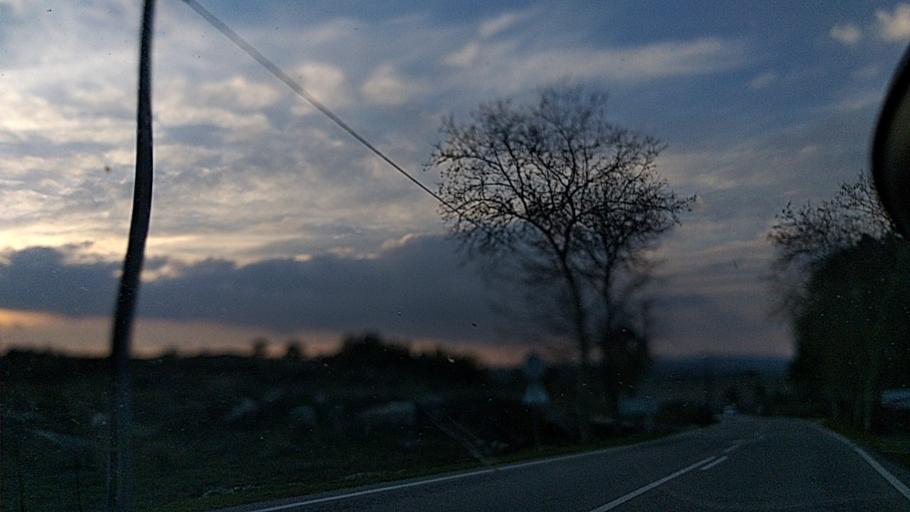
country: PT
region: Guarda
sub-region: Guarda
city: Sequeira
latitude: 40.5755
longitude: -7.1825
